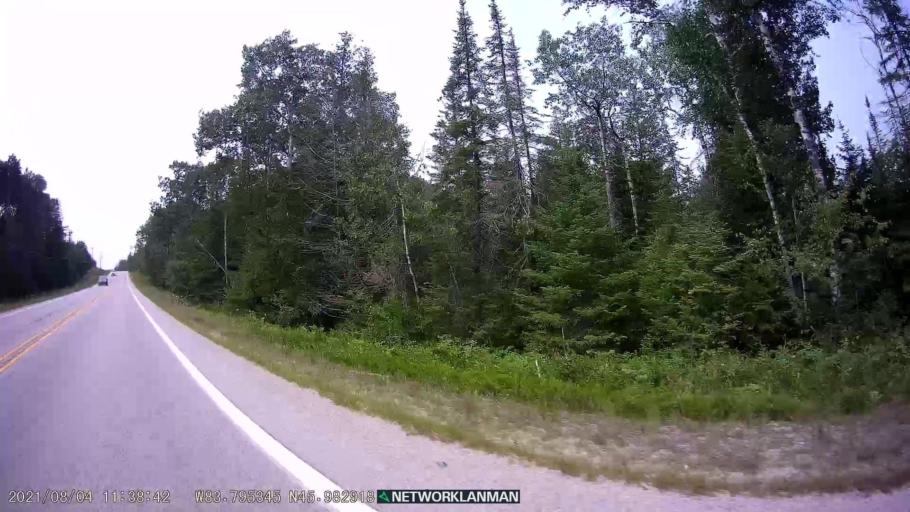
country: CA
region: Ontario
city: Thessalon
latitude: 45.9830
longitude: -83.7960
